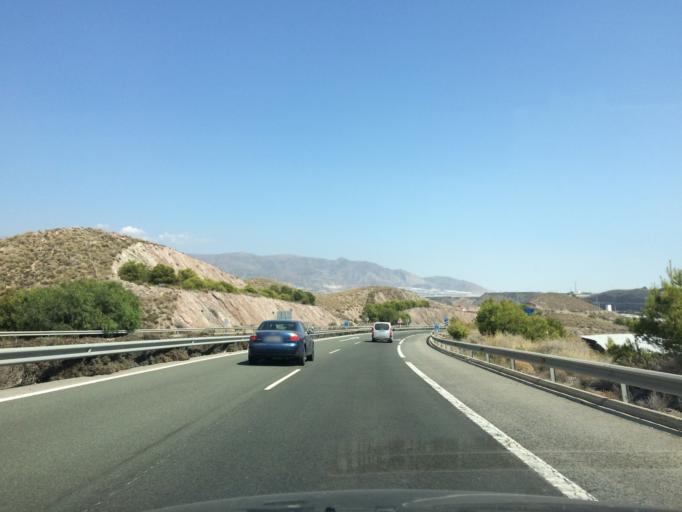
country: ES
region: Andalusia
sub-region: Provincia de Almeria
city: Adra
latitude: 36.7610
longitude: -3.0097
